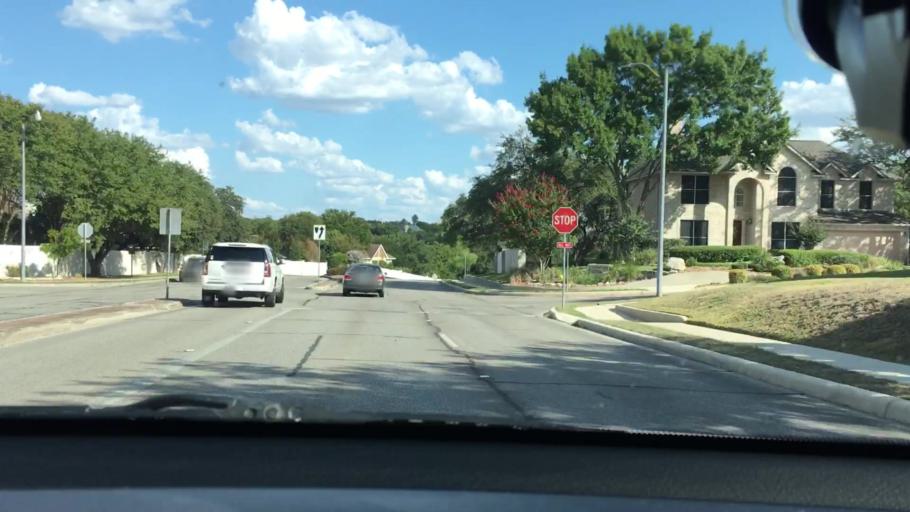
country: US
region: Texas
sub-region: Bexar County
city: Selma
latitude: 29.5666
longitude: -98.3135
